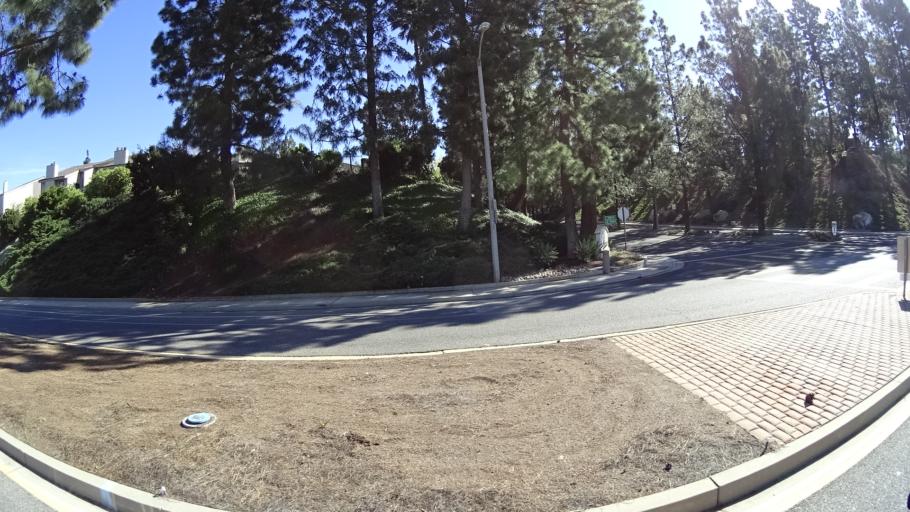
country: US
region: California
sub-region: Ventura County
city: Thousand Oaks
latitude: 34.2199
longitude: -118.8551
